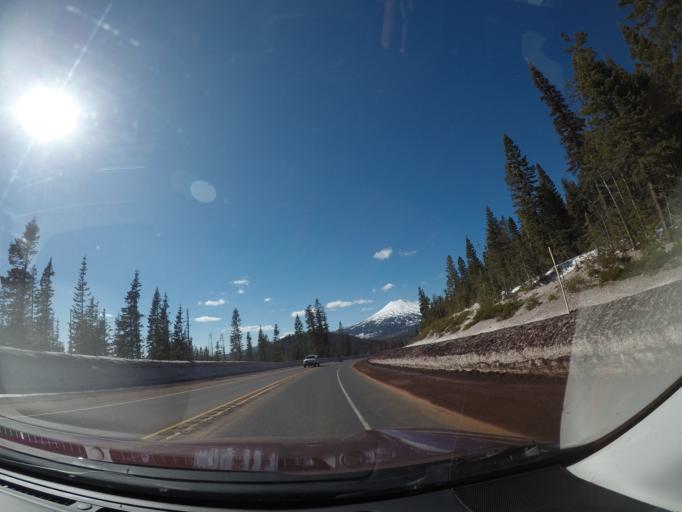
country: US
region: Oregon
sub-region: Deschutes County
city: Sunriver
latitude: 43.9803
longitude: -121.5851
